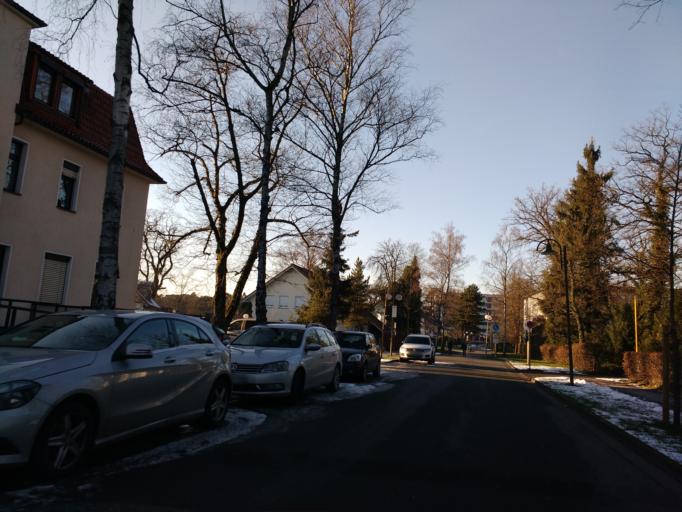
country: DE
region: North Rhine-Westphalia
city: Bad Lippspringe
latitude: 51.7848
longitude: 8.8127
